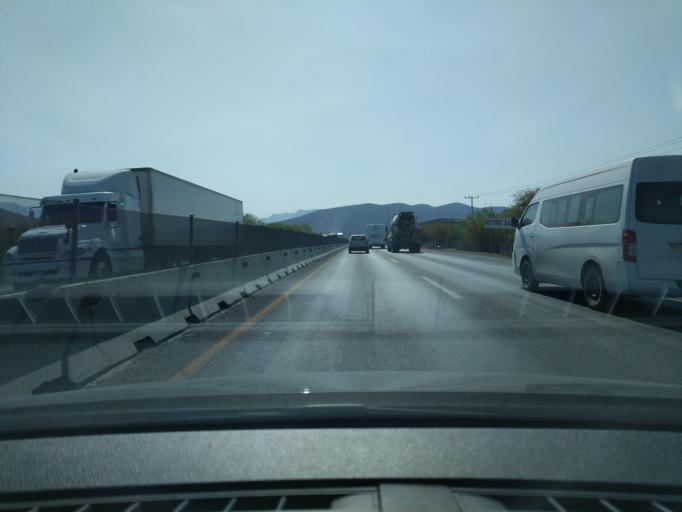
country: MX
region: Nuevo Leon
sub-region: Garcia
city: Los Parques
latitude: 25.7708
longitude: -100.4754
